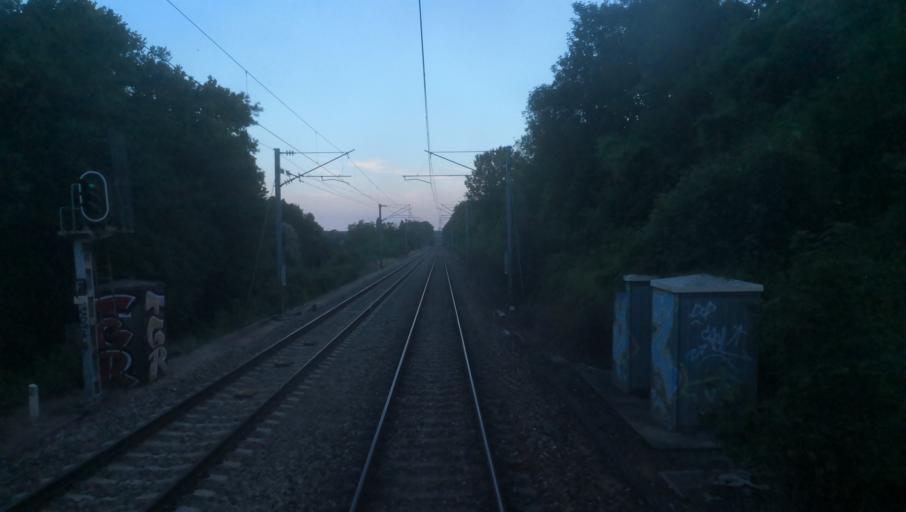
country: FR
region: Ile-de-France
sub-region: Departement des Yvelines
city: Breval
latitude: 48.9394
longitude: 1.5361
